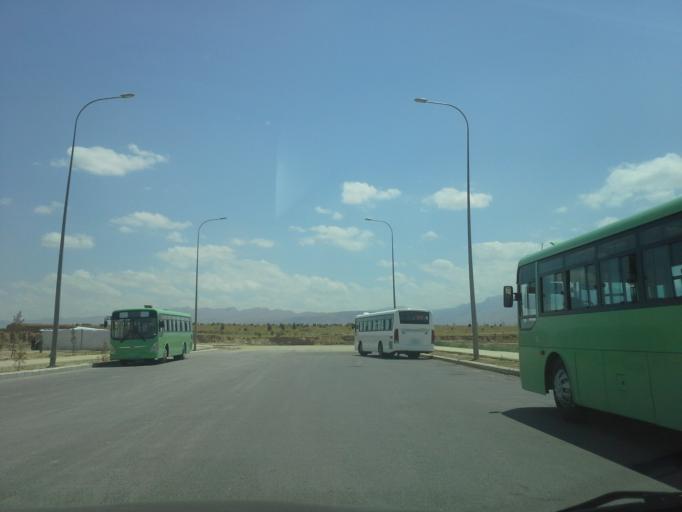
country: TM
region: Ahal
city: Ashgabat
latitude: 37.8862
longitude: 58.4054
